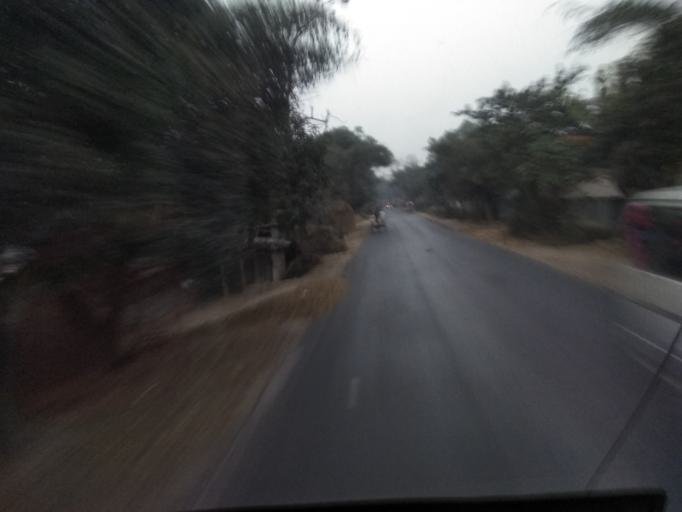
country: BD
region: Rajshahi
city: Bogra
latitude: 24.7493
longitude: 89.3416
